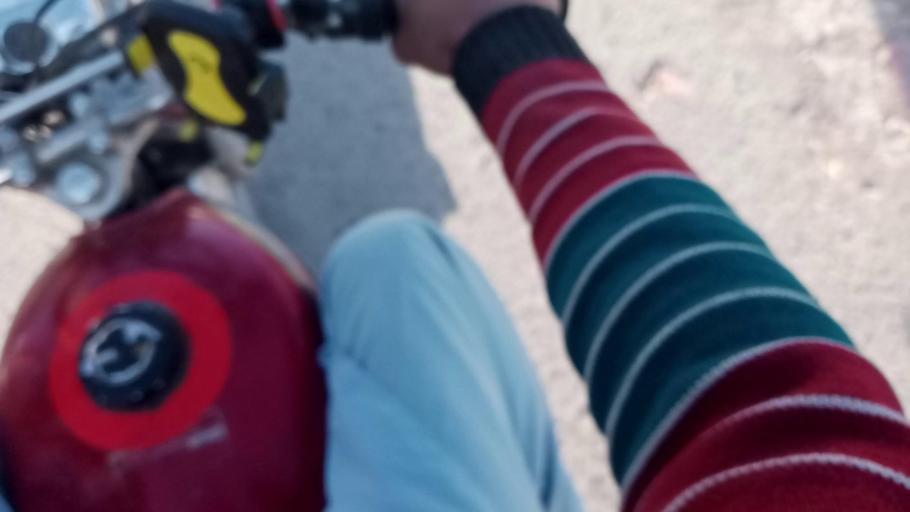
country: PK
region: Khyber Pakhtunkhwa
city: Peshawar
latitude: 34.0325
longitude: 71.6076
